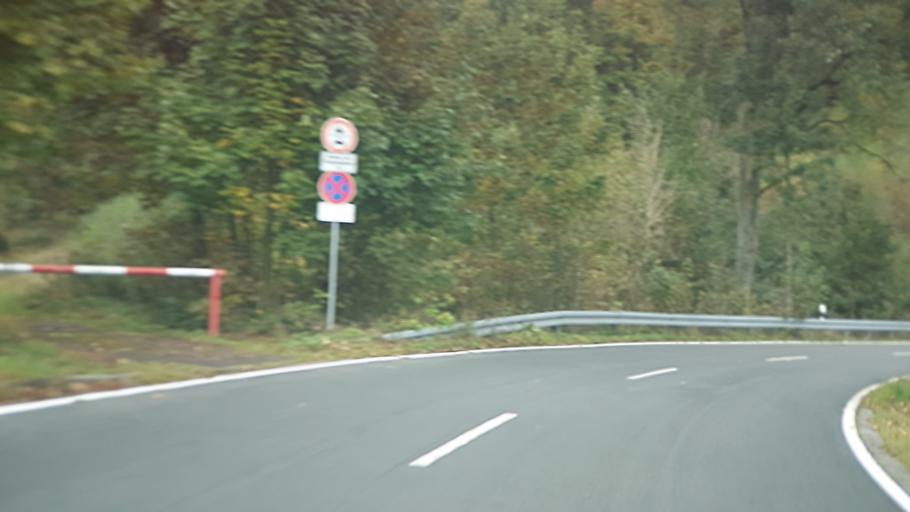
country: DE
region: North Rhine-Westphalia
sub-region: Regierungsbezirk Arnsberg
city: Luedenscheid
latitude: 51.1812
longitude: 7.6720
